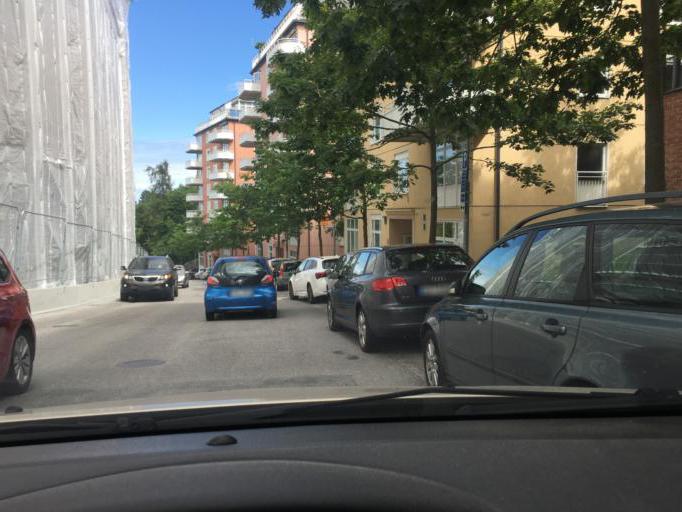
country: SE
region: Stockholm
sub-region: Nacka Kommun
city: Nacka
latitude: 59.3173
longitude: 18.1620
